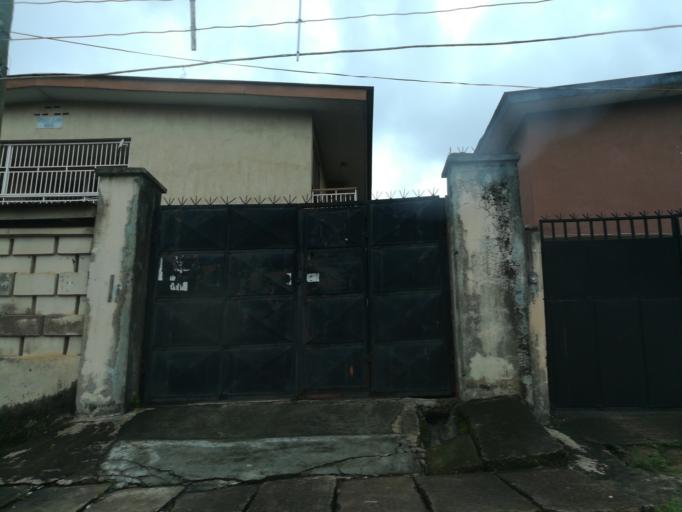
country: NG
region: Lagos
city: Agege
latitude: 6.6012
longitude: 3.3169
